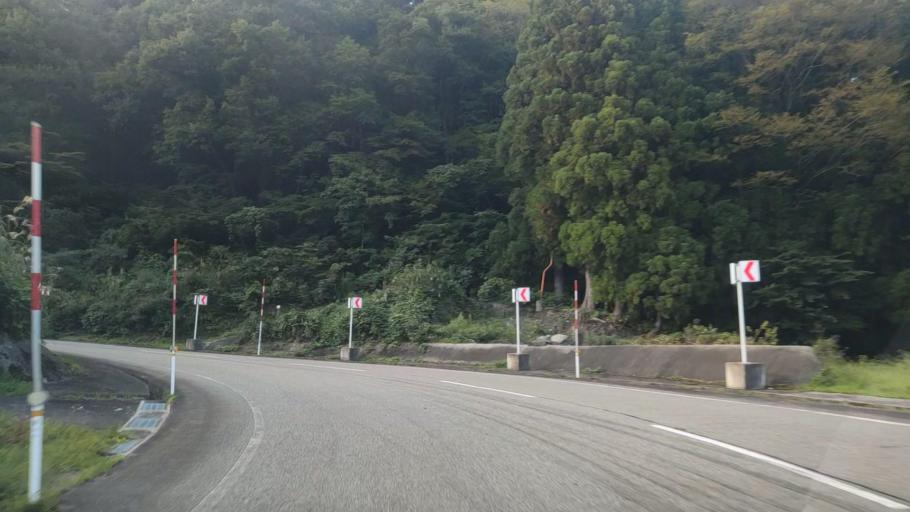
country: JP
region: Toyama
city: Yatsuomachi-higashikumisaka
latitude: 36.5058
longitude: 137.0631
